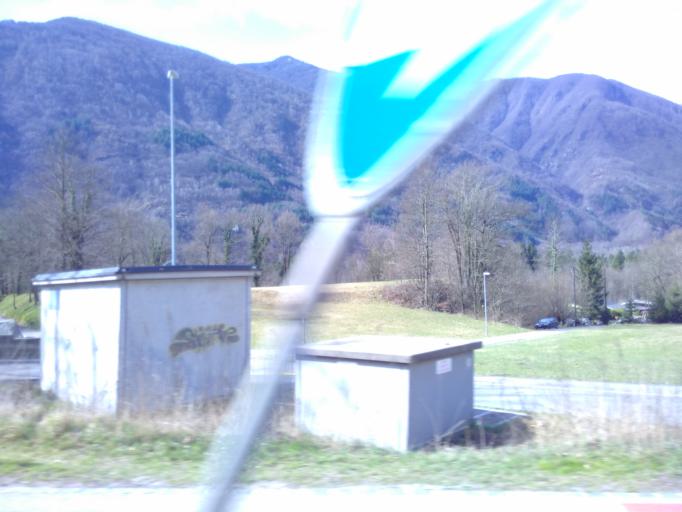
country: CH
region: Ticino
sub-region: Locarno District
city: Verscio
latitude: 46.2276
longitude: 8.7396
